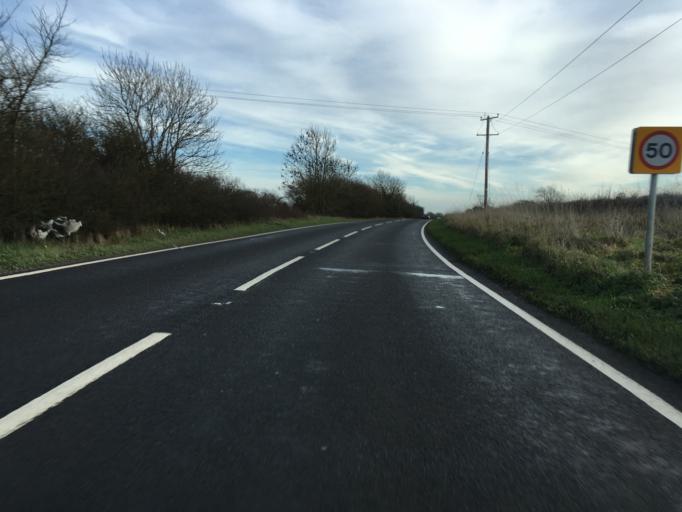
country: GB
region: England
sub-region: South Gloucestershire
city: Alveston
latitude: 51.5706
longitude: -2.5176
